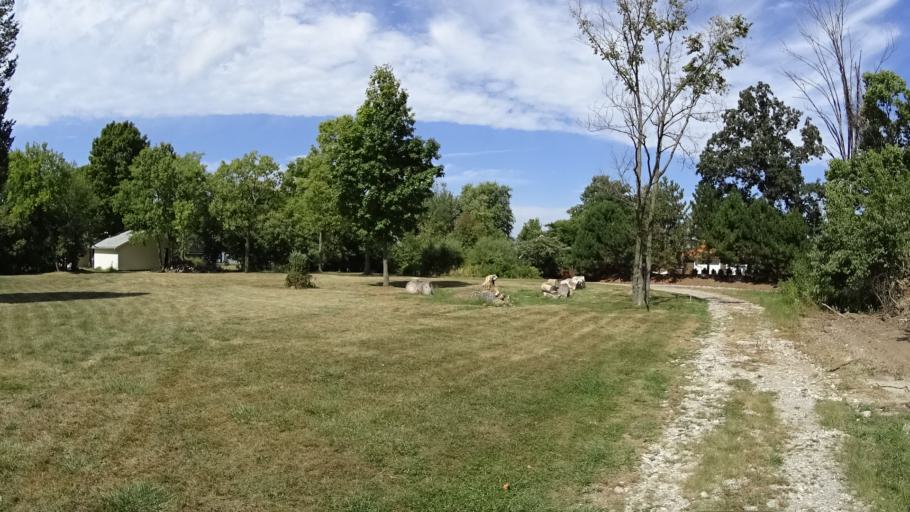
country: US
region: Ohio
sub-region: Erie County
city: Sandusky
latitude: 41.6094
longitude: -82.6935
